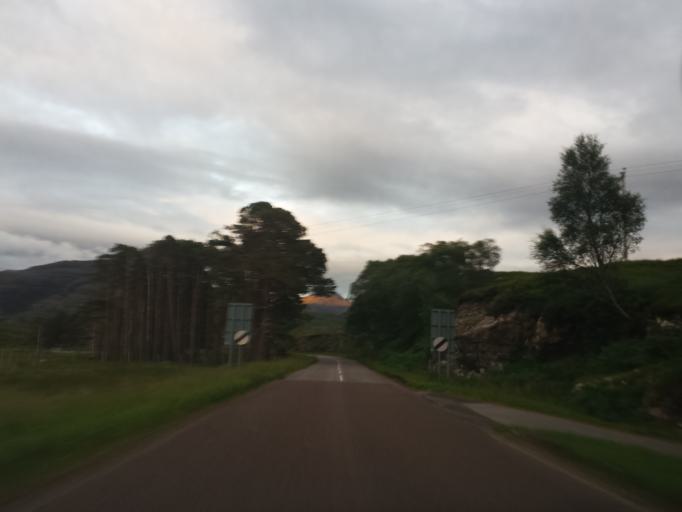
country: GB
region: Scotland
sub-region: Highland
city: Ullapool
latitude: 57.5336
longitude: -5.5111
